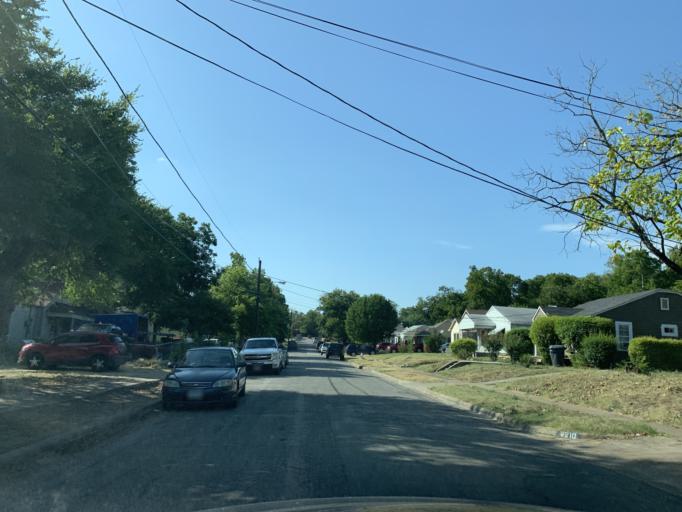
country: US
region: Texas
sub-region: Dallas County
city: Dallas
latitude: 32.6986
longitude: -96.7937
